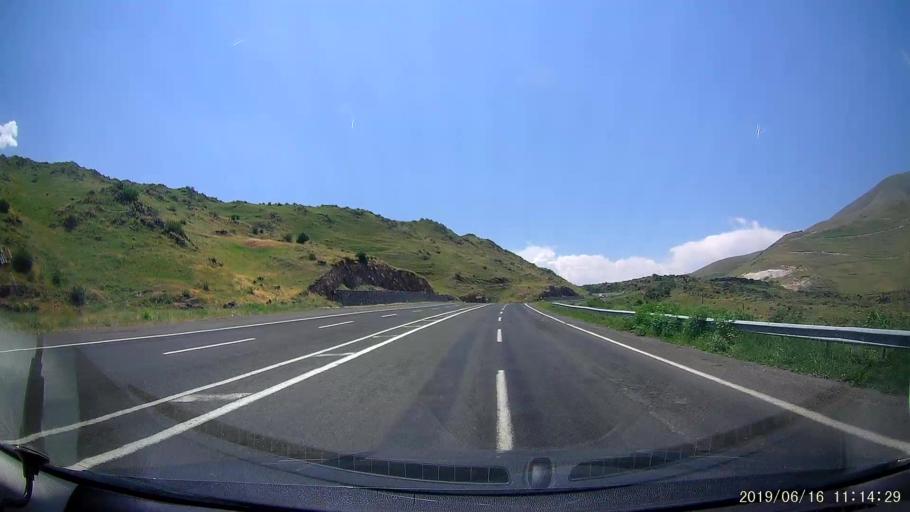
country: TR
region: Igdir
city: Igdir
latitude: 39.7780
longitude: 44.1422
